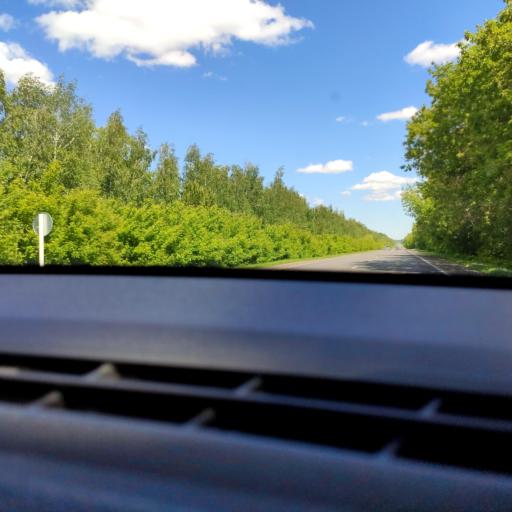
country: RU
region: Samara
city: Povolzhskiy
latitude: 53.6059
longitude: 49.6065
